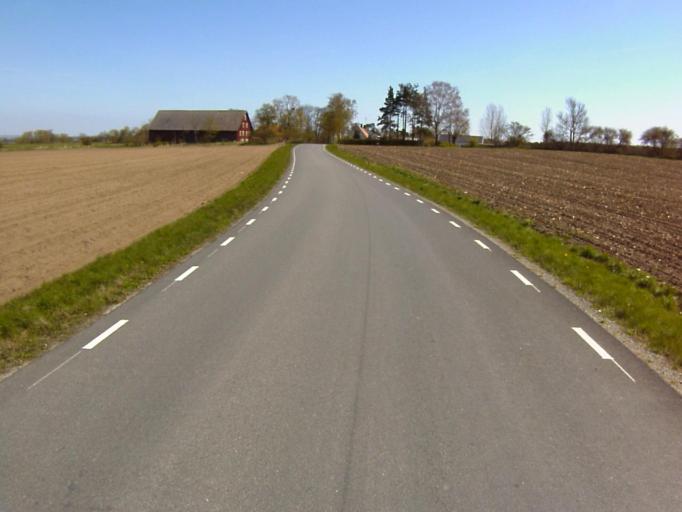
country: SE
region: Skane
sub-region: Kristianstads Kommun
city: Norra Asum
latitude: 55.9923
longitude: 14.1065
